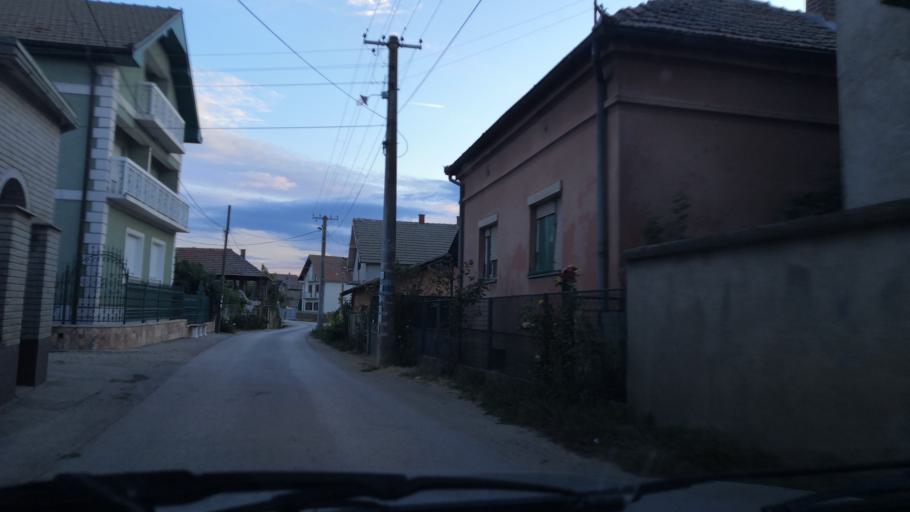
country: RO
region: Mehedinti
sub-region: Comuna Gogosu
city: Balta Verde
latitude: 44.2943
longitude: 22.5836
